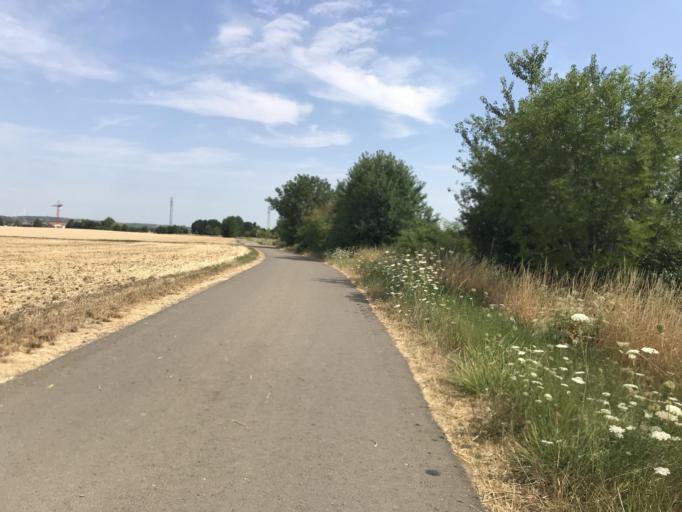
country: DE
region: Rheinland-Pfalz
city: Kongernheim
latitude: 49.8328
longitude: 8.2400
